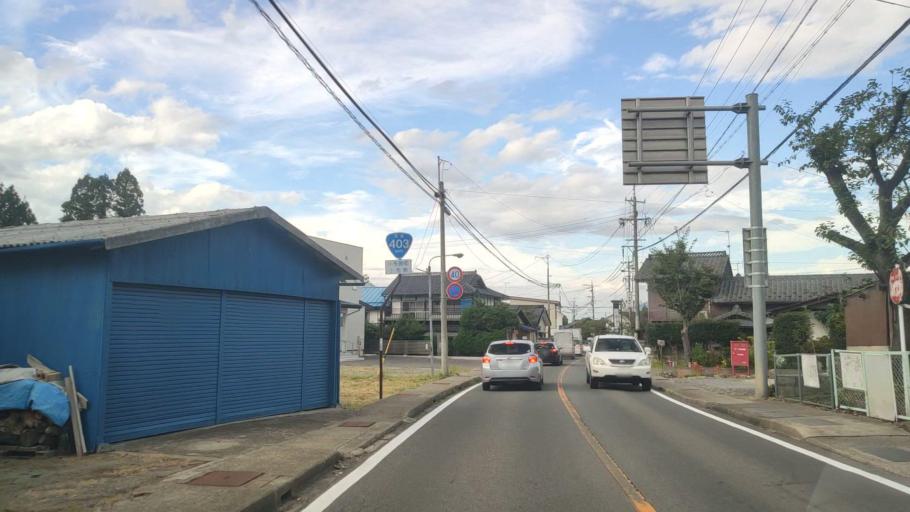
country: JP
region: Nagano
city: Suzaka
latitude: 36.6932
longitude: 138.3152
